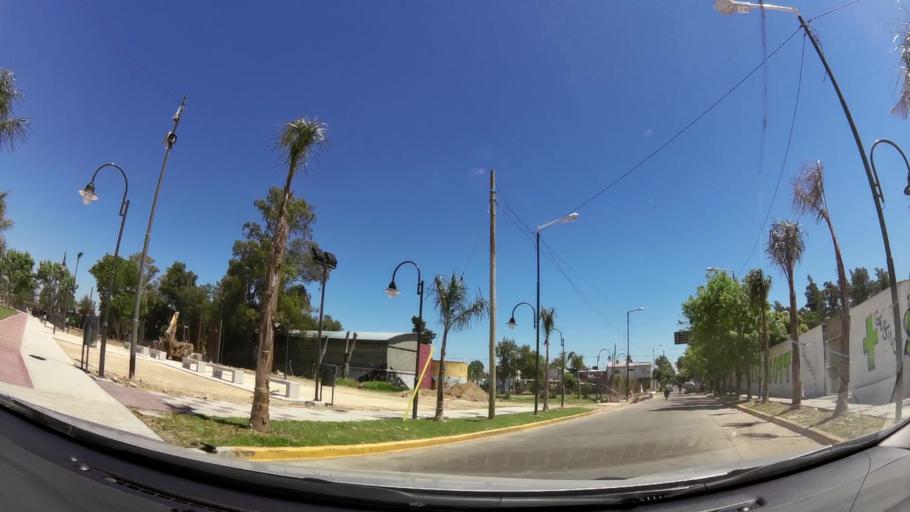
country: AR
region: Buenos Aires
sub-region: Partido de Tigre
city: Tigre
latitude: -34.4562
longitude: -58.5536
